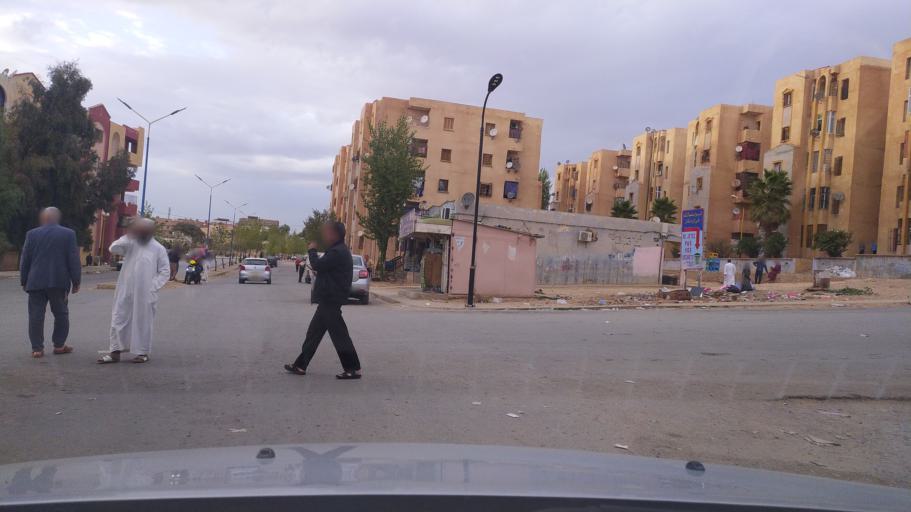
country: DZ
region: Tiaret
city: Frenda
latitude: 35.0567
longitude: 1.0614
